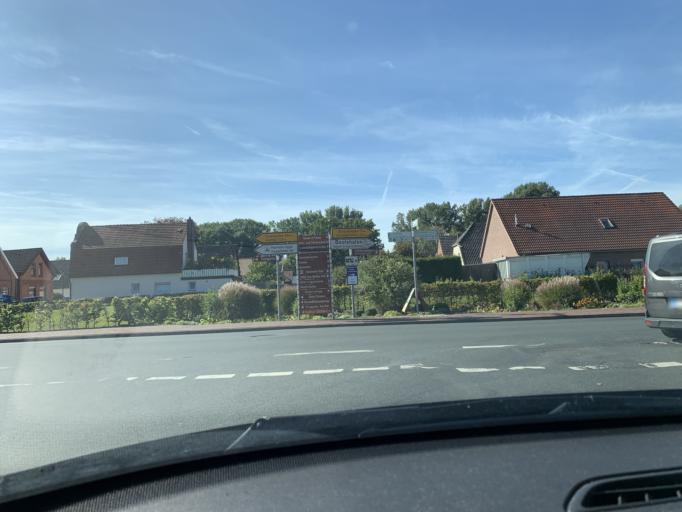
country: DE
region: Lower Saxony
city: Barssel
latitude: 53.1687
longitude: 7.7452
